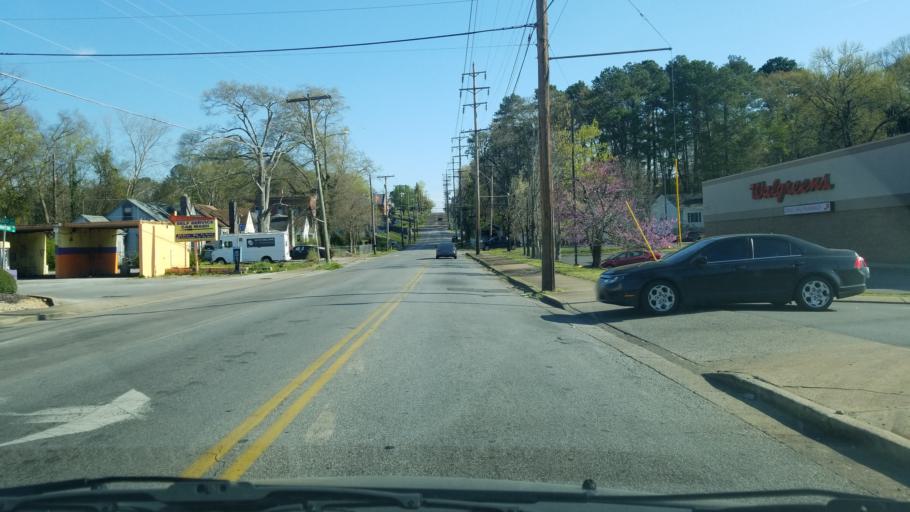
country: US
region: Tennessee
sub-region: Hamilton County
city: East Ridge
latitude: 35.0244
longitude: -85.2463
